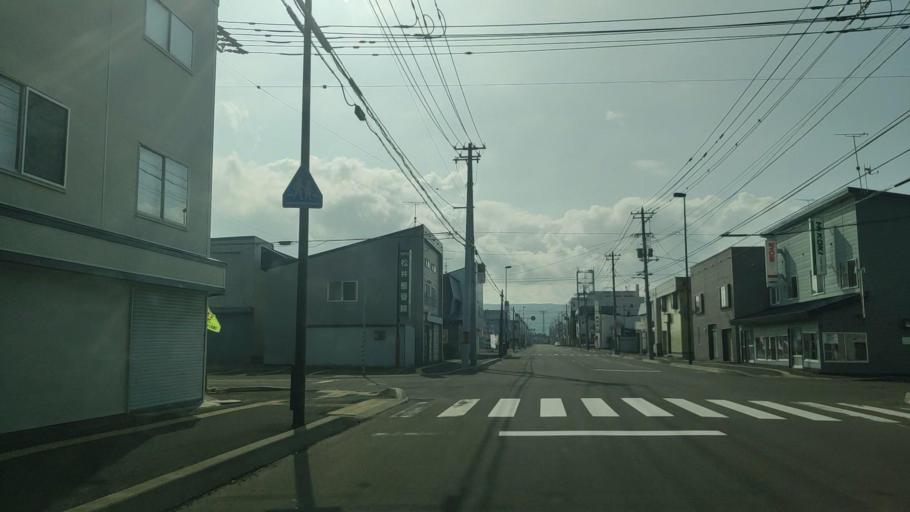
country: JP
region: Hokkaido
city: Shimo-furano
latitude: 43.3486
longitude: 142.3857
